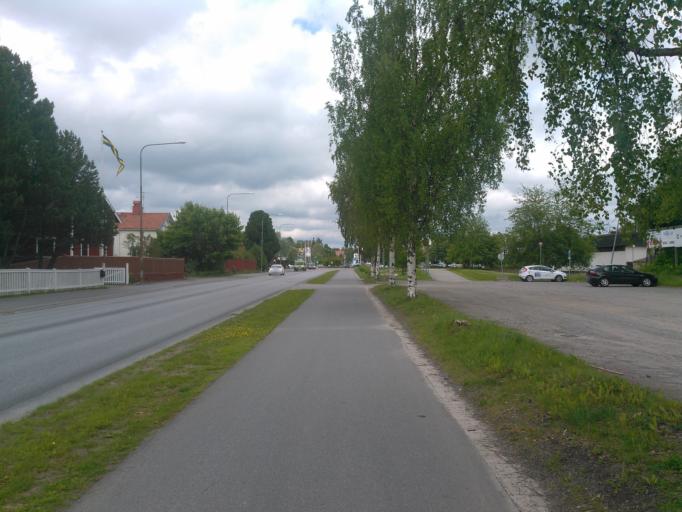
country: SE
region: Vaesterbotten
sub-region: Umea Kommun
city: Umea
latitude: 63.8309
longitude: 20.2834
